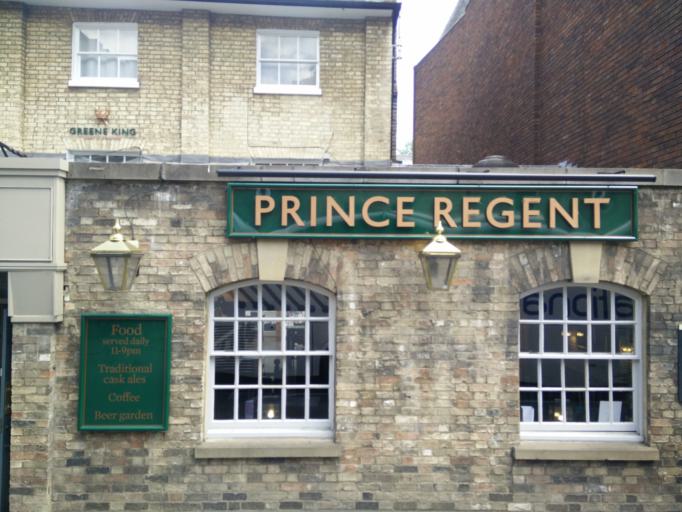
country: GB
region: England
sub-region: Cambridgeshire
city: Cambridge
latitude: 52.1999
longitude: 0.1268
